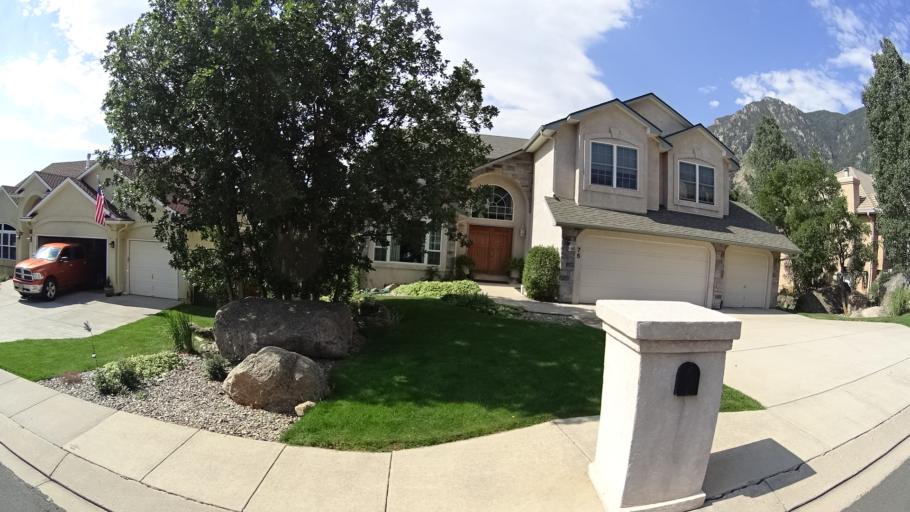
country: US
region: Colorado
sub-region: El Paso County
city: Fort Carson
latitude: 38.7507
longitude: -104.8352
